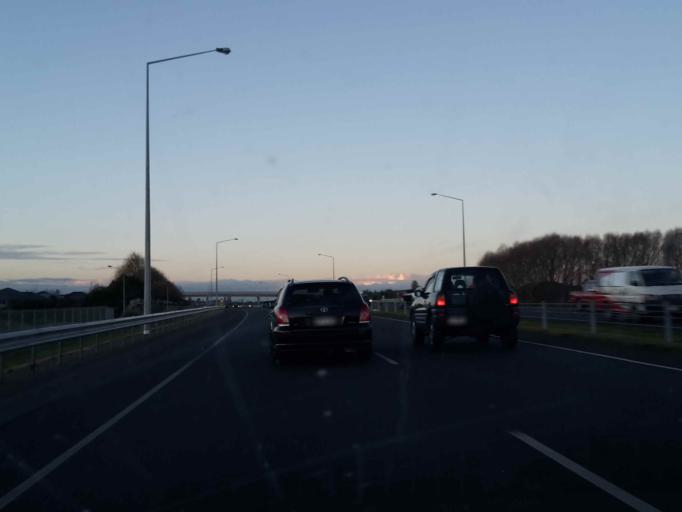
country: NZ
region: Canterbury
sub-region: Selwyn District
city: Prebbleton
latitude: -43.5620
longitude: 172.5599
